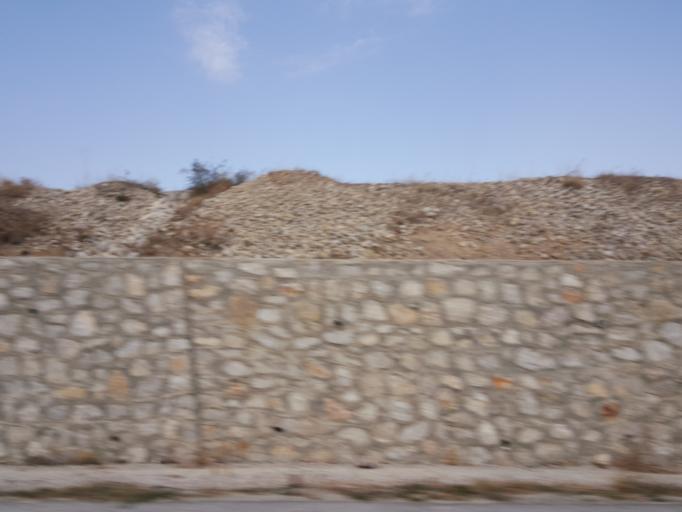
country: TR
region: Corum
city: Alaca
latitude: 40.1391
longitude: 34.8040
